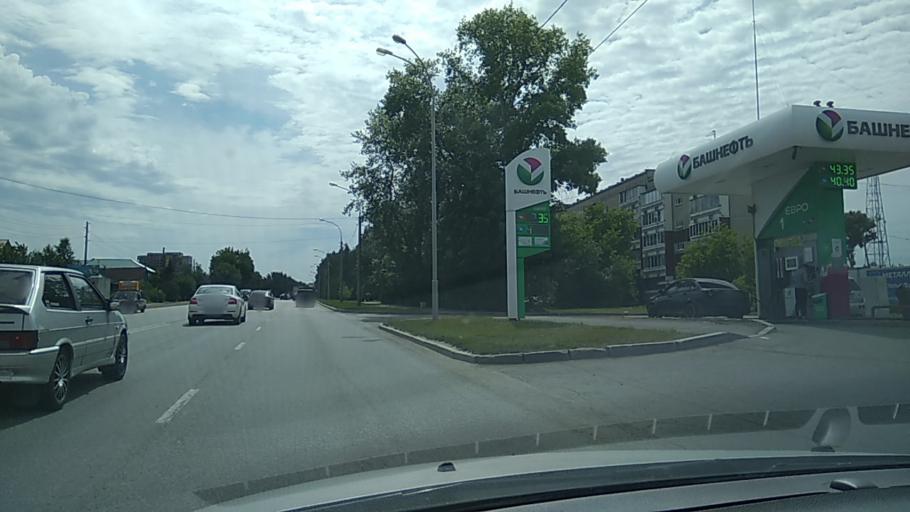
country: RU
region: Sverdlovsk
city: Verkhnyaya Pyshma
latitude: 56.9276
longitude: 60.6138
